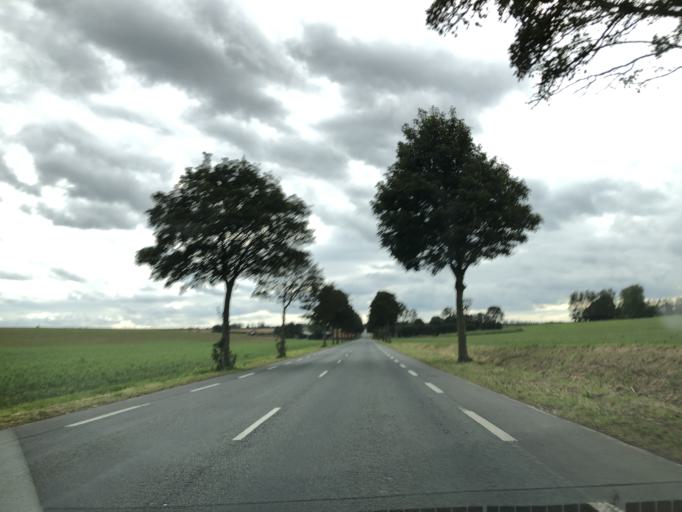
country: FR
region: Nord-Pas-de-Calais
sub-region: Departement du Pas-de-Calais
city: Auchy-les-Hesdin
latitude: 50.4390
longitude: 2.0749
